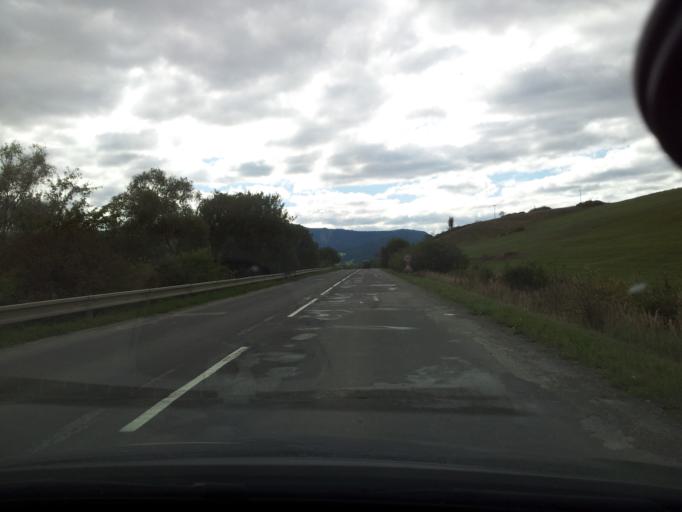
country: SK
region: Zilinsky
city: Ruzomberok
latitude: 49.0914
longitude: 19.4351
